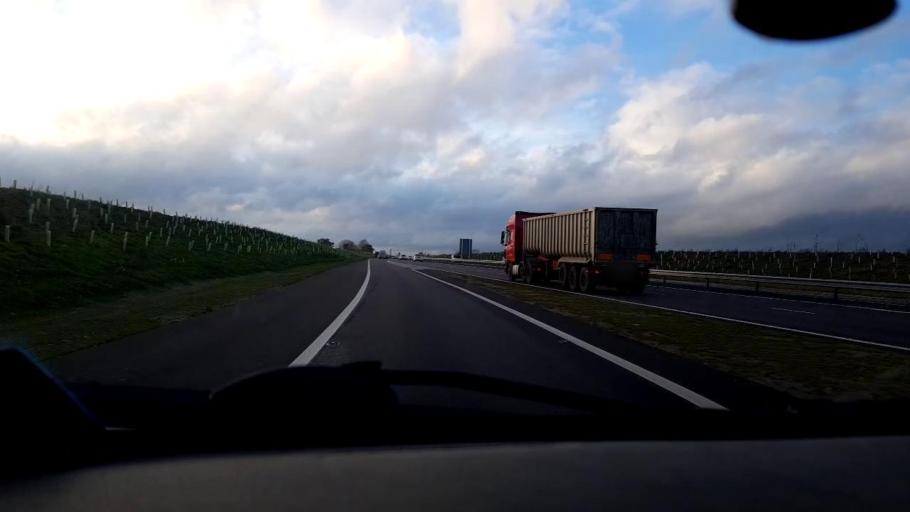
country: GB
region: England
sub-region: Norfolk
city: Horsford
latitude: 52.6817
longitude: 1.2573
